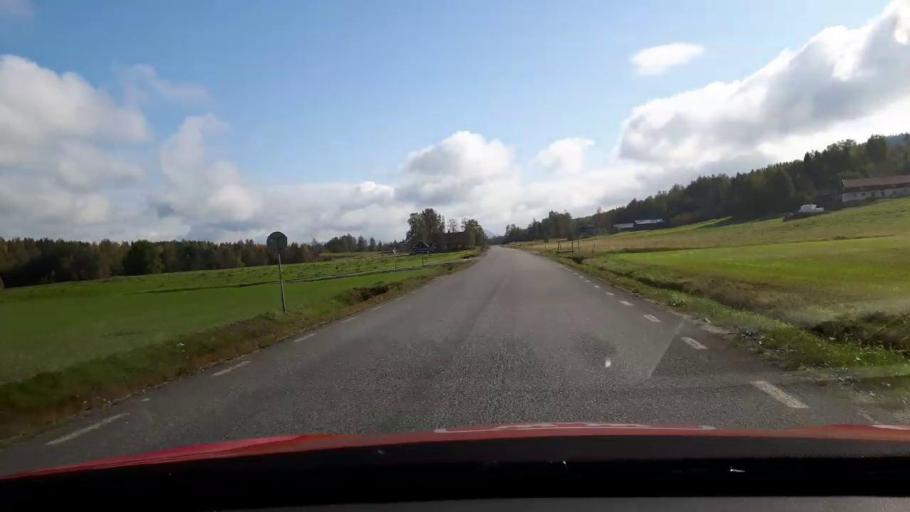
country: SE
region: Gaevleborg
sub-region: Ljusdals Kommun
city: Ljusdal
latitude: 61.7665
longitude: 16.0411
